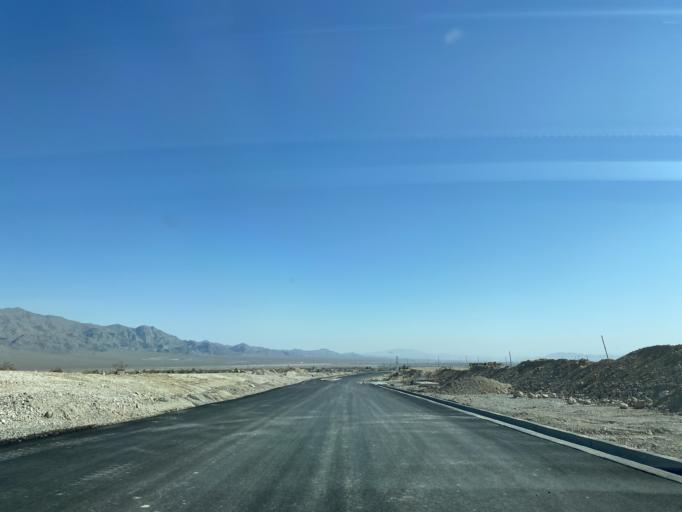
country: US
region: Nevada
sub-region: Clark County
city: Summerlin South
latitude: 36.3213
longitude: -115.3184
